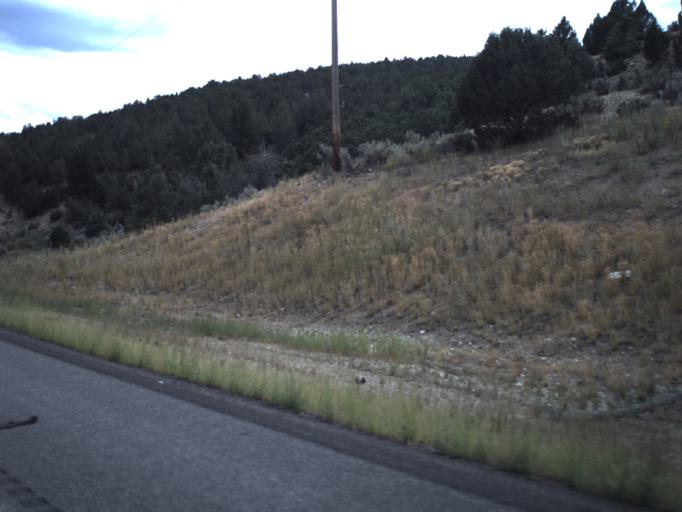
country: US
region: Utah
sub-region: Sanpete County
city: Fairview
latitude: 39.9484
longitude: -111.2152
